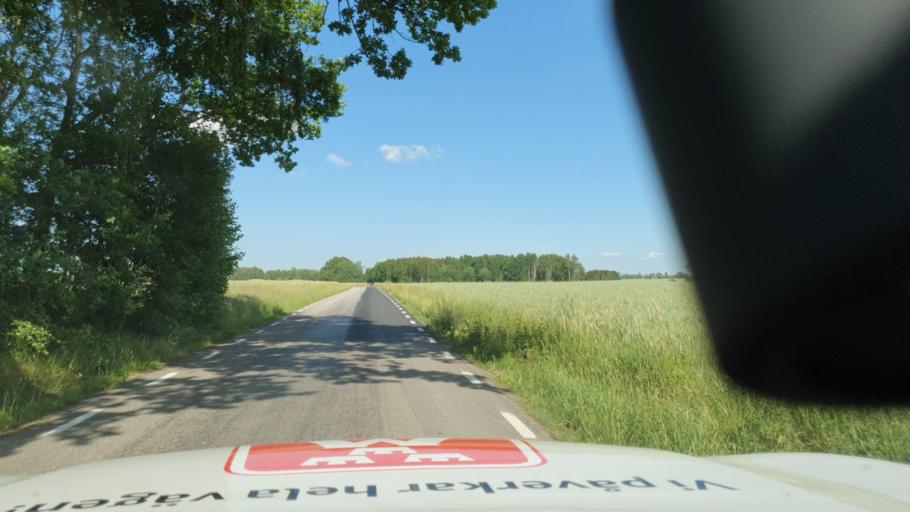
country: SE
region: Vaestra Goetaland
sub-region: Lidkopings Kommun
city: Lidkoping
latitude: 58.4270
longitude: 13.1400
